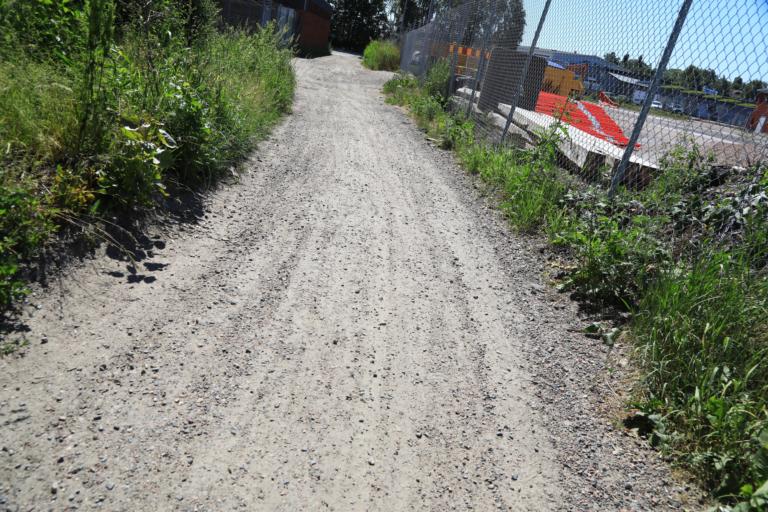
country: SE
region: Halland
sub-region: Kungsbacka Kommun
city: Kungsbacka
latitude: 57.5066
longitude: 12.0696
